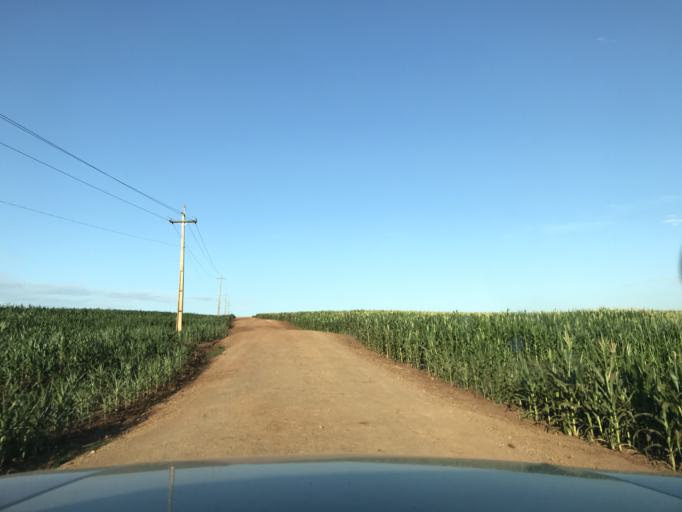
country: BR
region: Parana
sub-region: Palotina
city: Palotina
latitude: -24.2537
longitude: -53.7260
